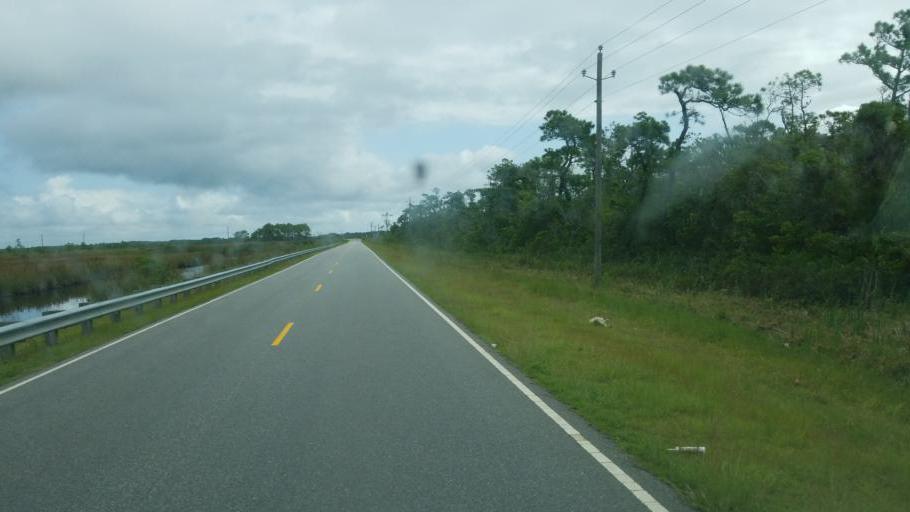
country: US
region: North Carolina
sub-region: Dare County
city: Manteo
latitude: 35.8672
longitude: -75.7885
